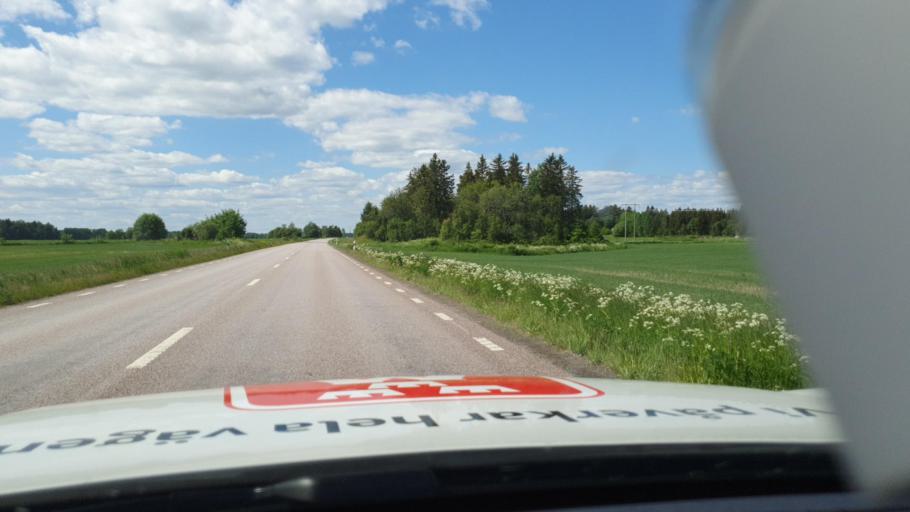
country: SE
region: Uppsala
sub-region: Tierps Kommun
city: Karlholmsbruk
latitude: 60.4880
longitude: 17.7310
